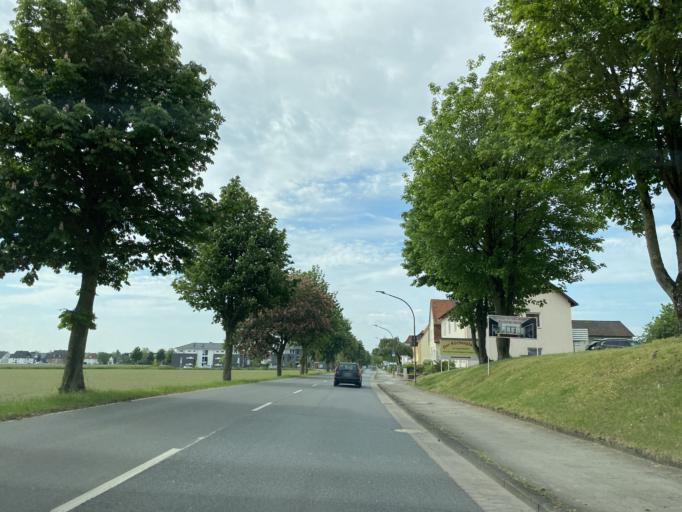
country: DE
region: Lower Saxony
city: Bad Rothenfelde
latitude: 52.1187
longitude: 8.1645
